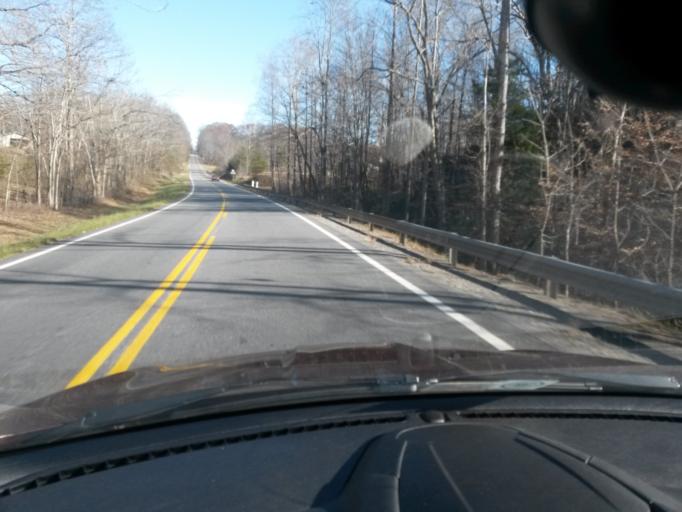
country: US
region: Virginia
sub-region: Patrick County
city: Patrick Springs
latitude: 36.7575
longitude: -80.1807
